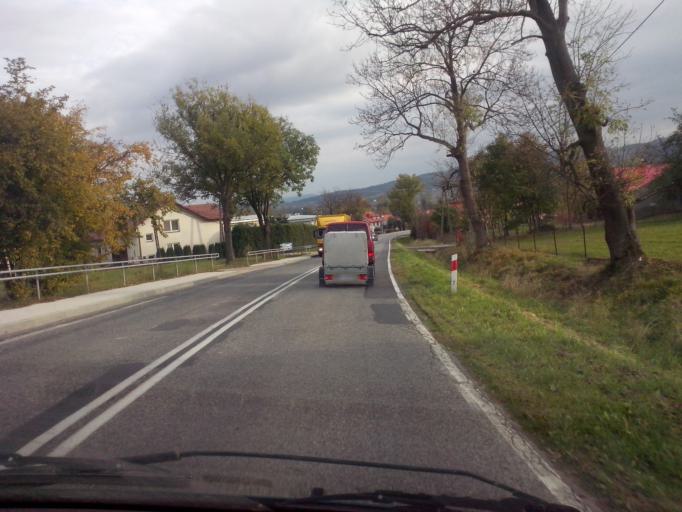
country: PL
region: Subcarpathian Voivodeship
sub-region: Powiat strzyzowski
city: Wisniowa
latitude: 49.8728
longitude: 21.6579
